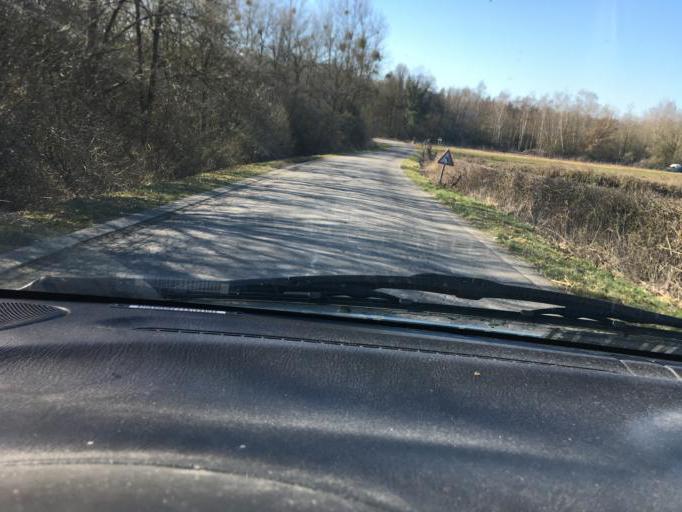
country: BE
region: Wallonia
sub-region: Province de Namur
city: Doische
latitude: 50.1637
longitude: 4.7310
